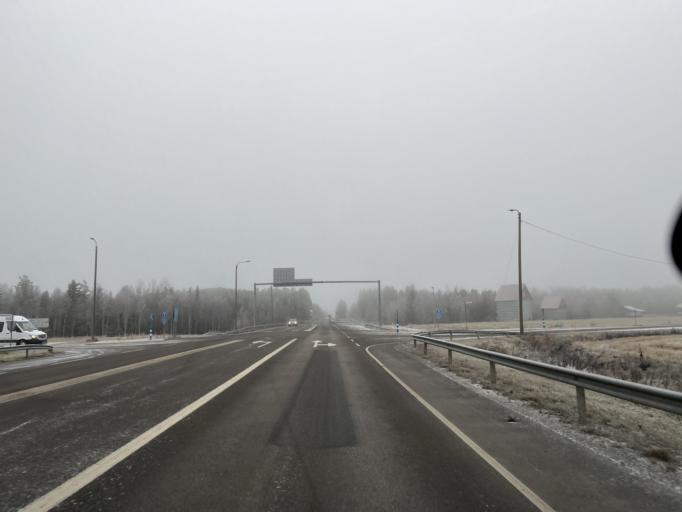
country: FI
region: Northern Ostrobothnia
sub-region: Raahe
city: Ruukki
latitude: 64.7206
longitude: 24.9847
